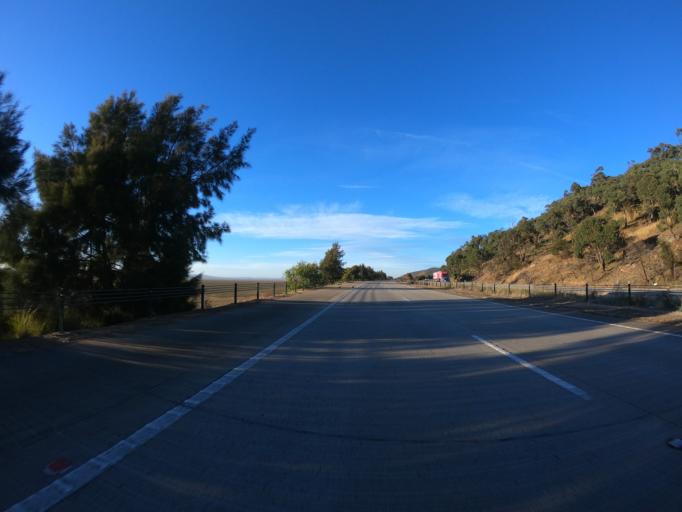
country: AU
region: New South Wales
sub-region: Yass Valley
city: Gundaroo
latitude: -35.0903
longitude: 149.3751
